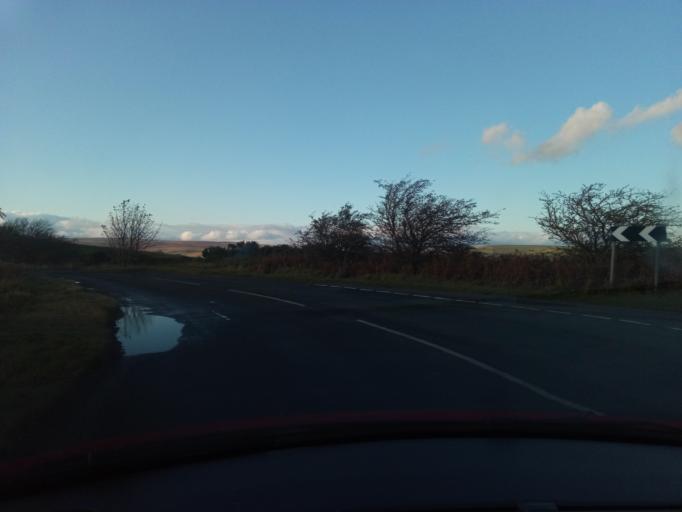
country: GB
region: England
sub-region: County Durham
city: Wolsingham
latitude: 54.7125
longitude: -1.8742
